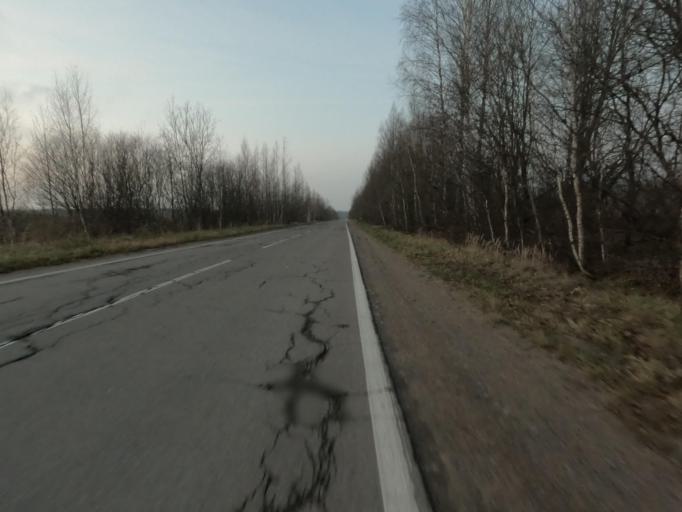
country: RU
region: Leningrad
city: Kirovsk
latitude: 59.8599
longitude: 30.9811
